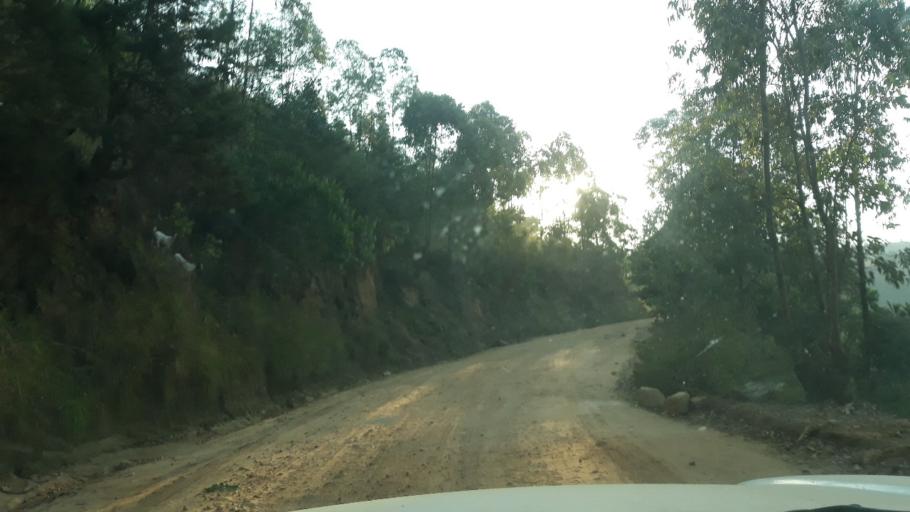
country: RW
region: Western Province
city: Cyangugu
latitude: -2.6989
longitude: 28.9036
